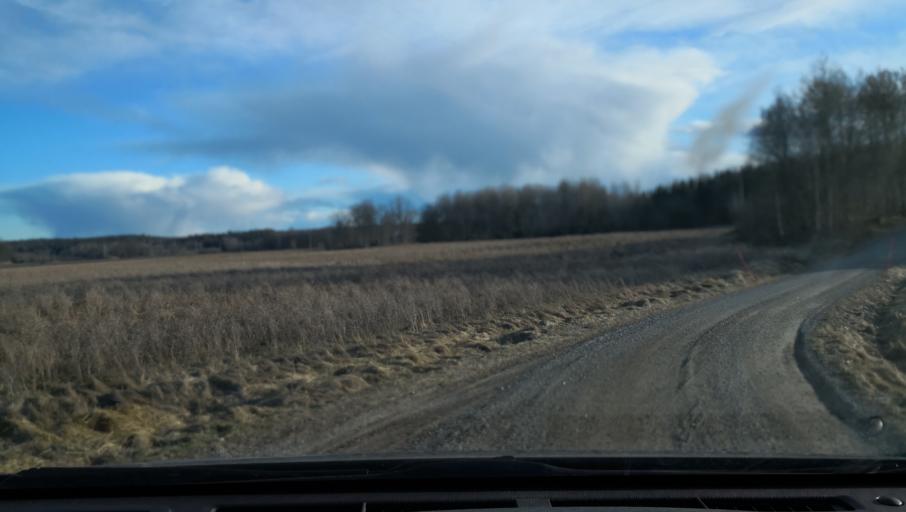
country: SE
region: Vaestmanland
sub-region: Arboga Kommun
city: Arboga
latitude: 59.4201
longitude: 15.7469
